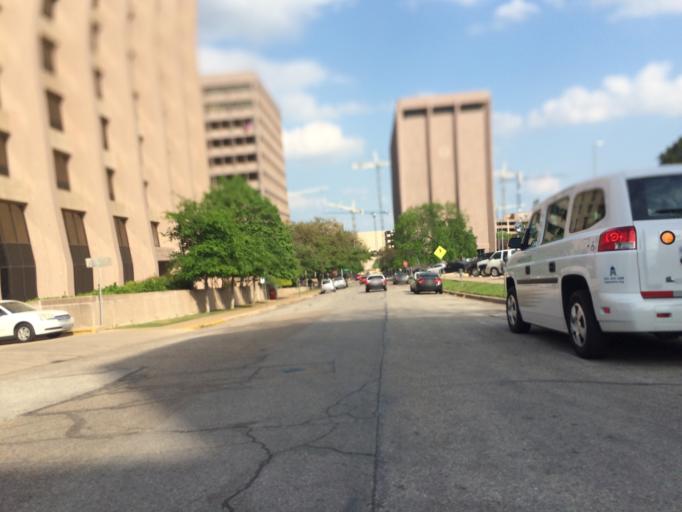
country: US
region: Texas
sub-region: Travis County
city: Austin
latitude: 30.2791
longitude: -97.7402
